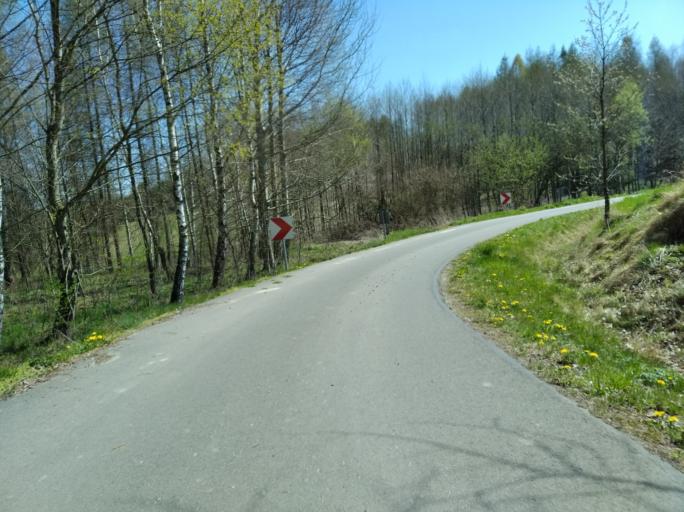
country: PL
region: Subcarpathian Voivodeship
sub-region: Powiat strzyzowski
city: Wisniowa
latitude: 49.9048
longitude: 21.6814
